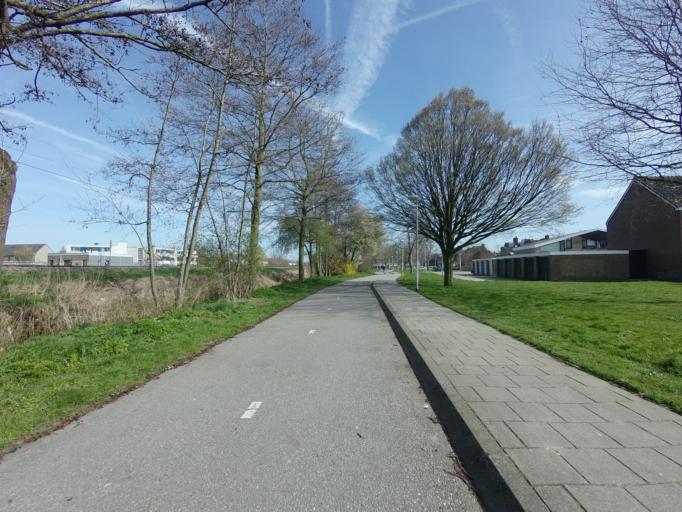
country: NL
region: South Holland
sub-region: Bodegraven-Reeuwijk
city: Bodegraven
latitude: 52.0797
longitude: 4.7540
